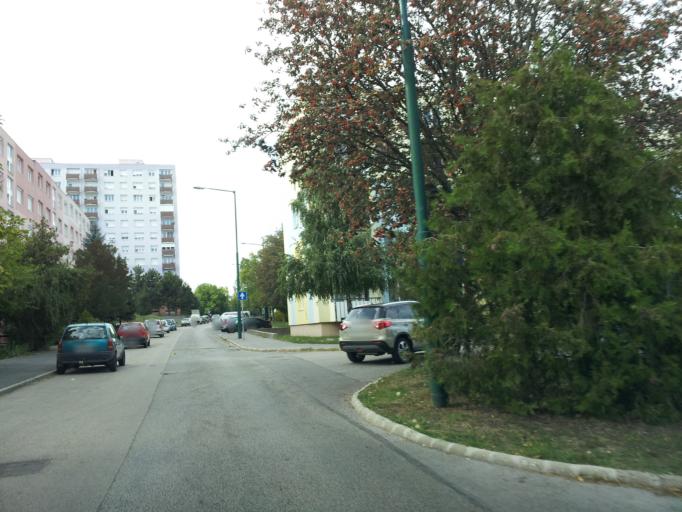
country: HU
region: Pest
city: Szazhalombatta
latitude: 47.3130
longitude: 18.9091
